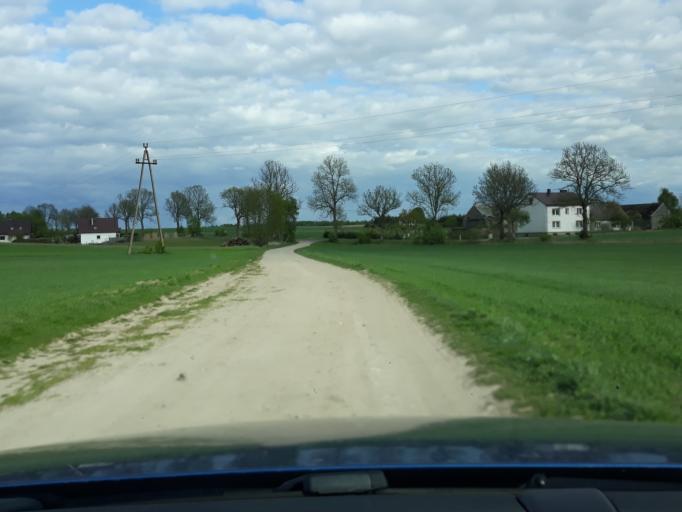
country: PL
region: Pomeranian Voivodeship
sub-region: Powiat czluchowski
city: Czluchow
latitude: 53.7524
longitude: 17.3755
